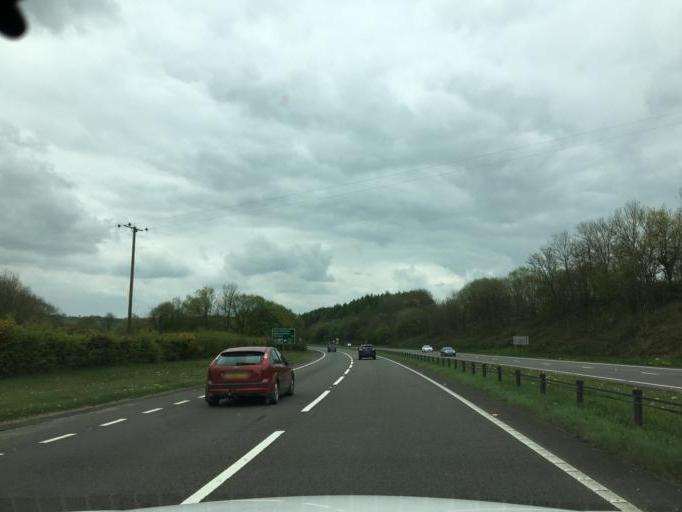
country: GB
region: Wales
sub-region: Carmarthenshire
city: Cross Hands
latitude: 51.7610
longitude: -4.0697
